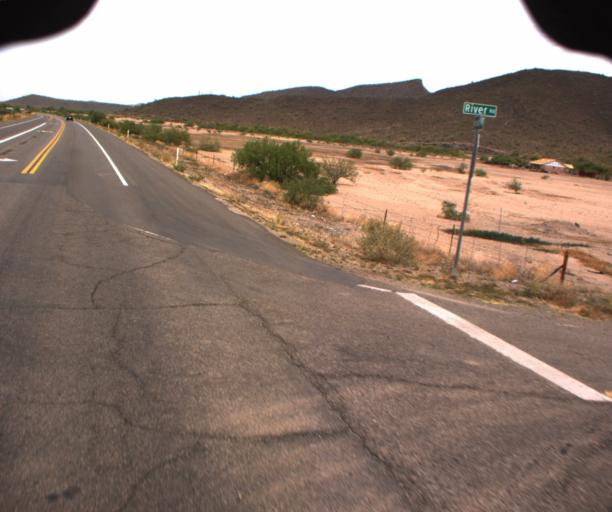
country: US
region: Arizona
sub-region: Pinal County
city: Sacaton
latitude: 33.1031
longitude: -111.7132
